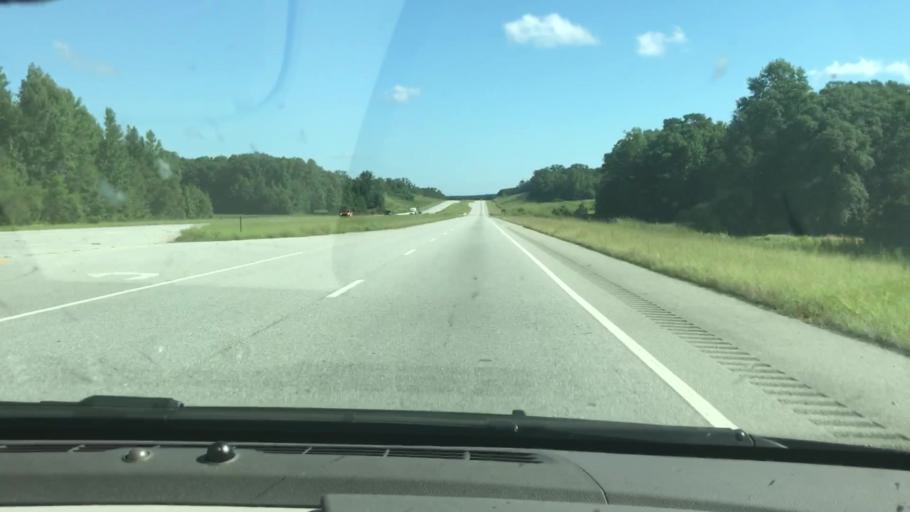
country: US
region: Alabama
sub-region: Russell County
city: Ladonia
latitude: 32.1983
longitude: -85.1777
